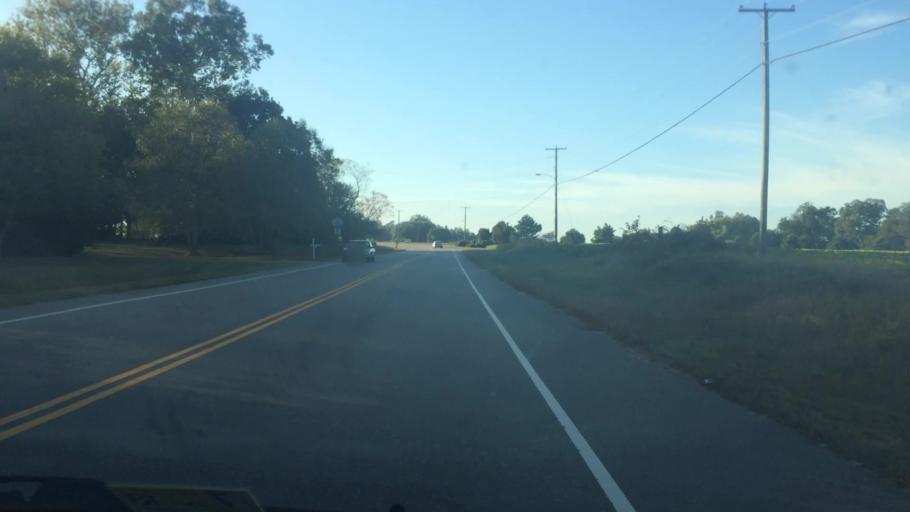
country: US
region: Virginia
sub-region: James City County
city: Williamsburg
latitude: 37.3815
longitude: -76.8041
